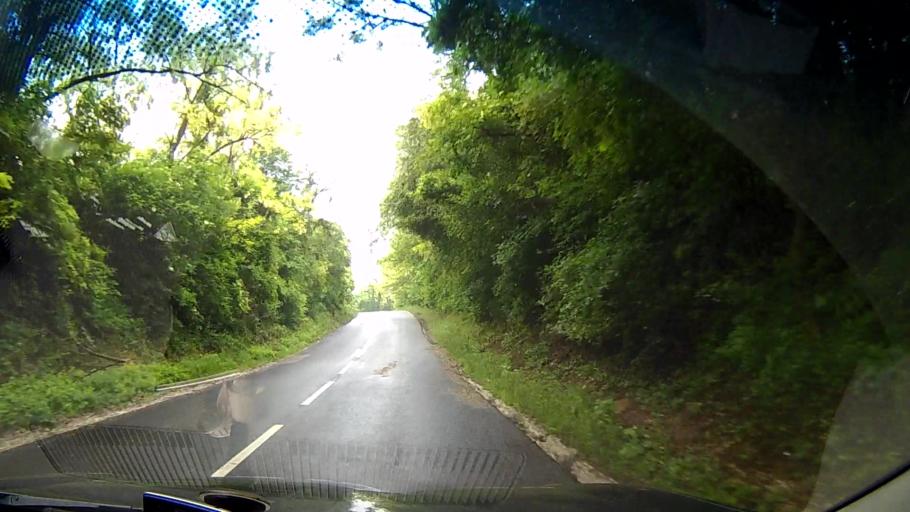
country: HU
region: Pest
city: Piliscsaba
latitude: 47.6395
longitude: 18.7844
